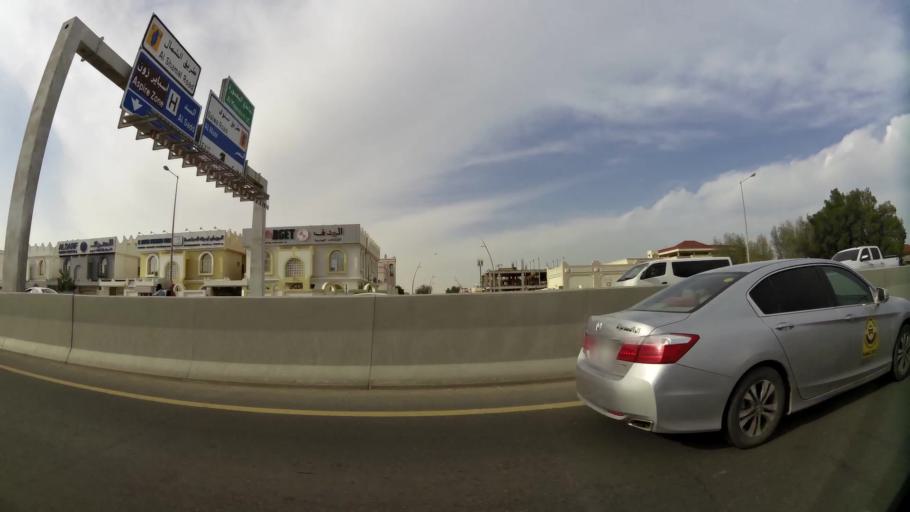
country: QA
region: Baladiyat ad Dawhah
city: Doha
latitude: 25.2543
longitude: 51.5148
